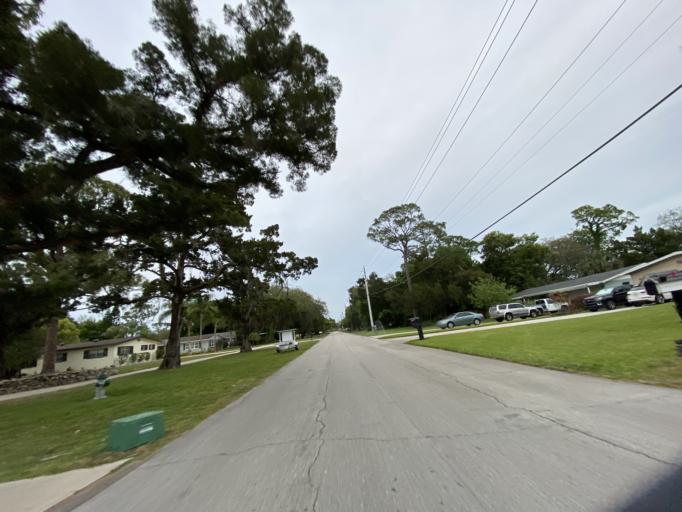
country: US
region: Florida
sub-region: Volusia County
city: South Daytona
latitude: 29.1645
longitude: -81.0073
